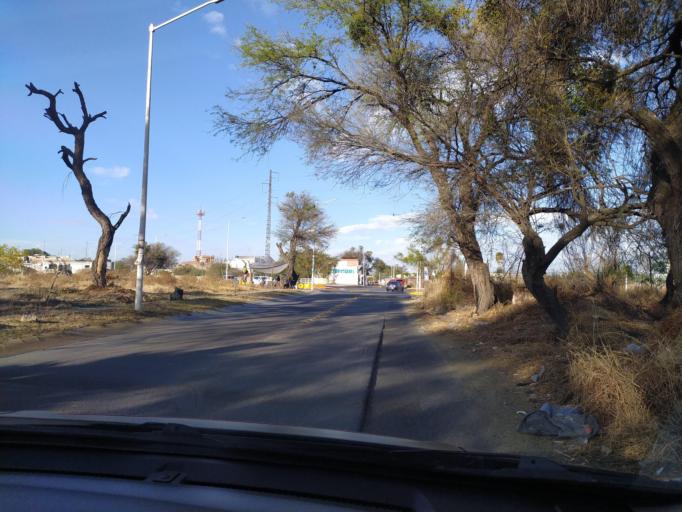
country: MX
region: Guanajuato
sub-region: Purisima del Rincon
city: Monte Grande
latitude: 21.0074
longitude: -101.8706
